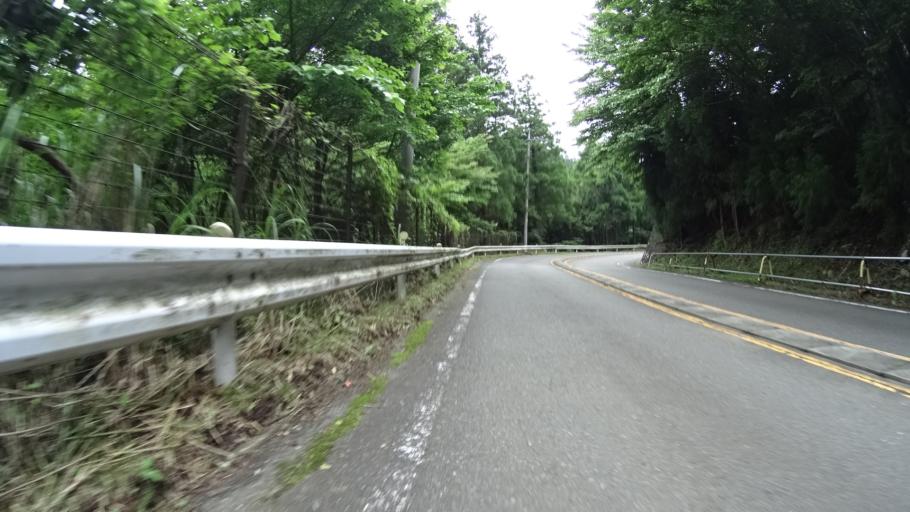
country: JP
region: Kanagawa
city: Hadano
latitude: 35.4993
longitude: 139.2314
